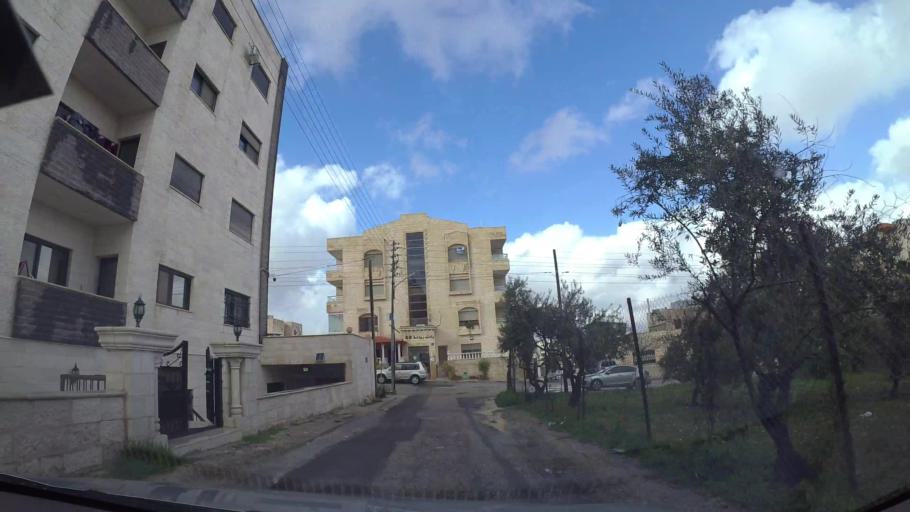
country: JO
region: Amman
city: Al Jubayhah
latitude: 32.0311
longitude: 35.8657
